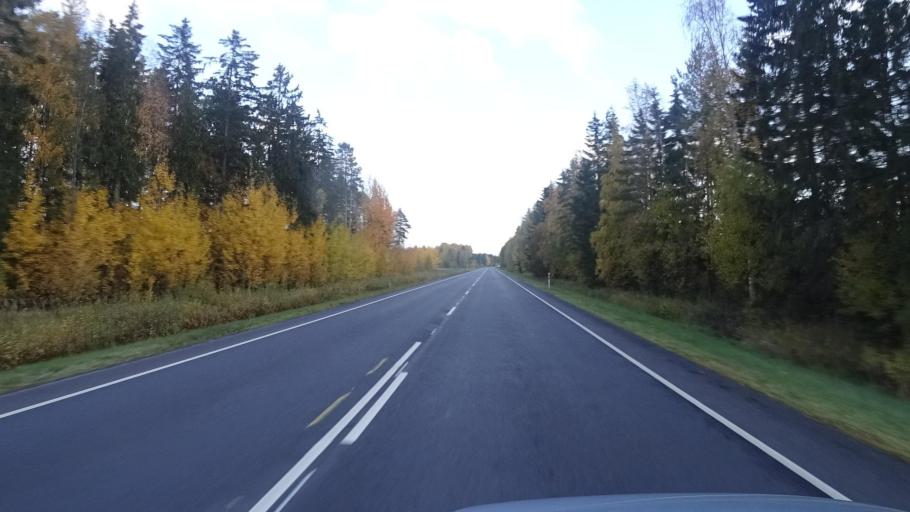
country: FI
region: Satakunta
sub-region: Rauma
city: Koeylioe
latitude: 61.0869
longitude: 22.2572
